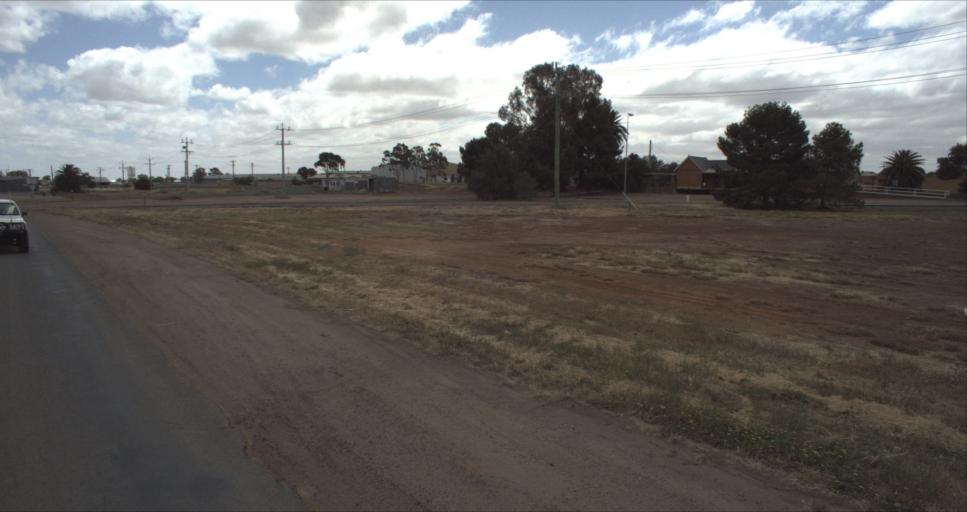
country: AU
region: New South Wales
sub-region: Leeton
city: Leeton
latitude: -34.5554
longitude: 146.3975
